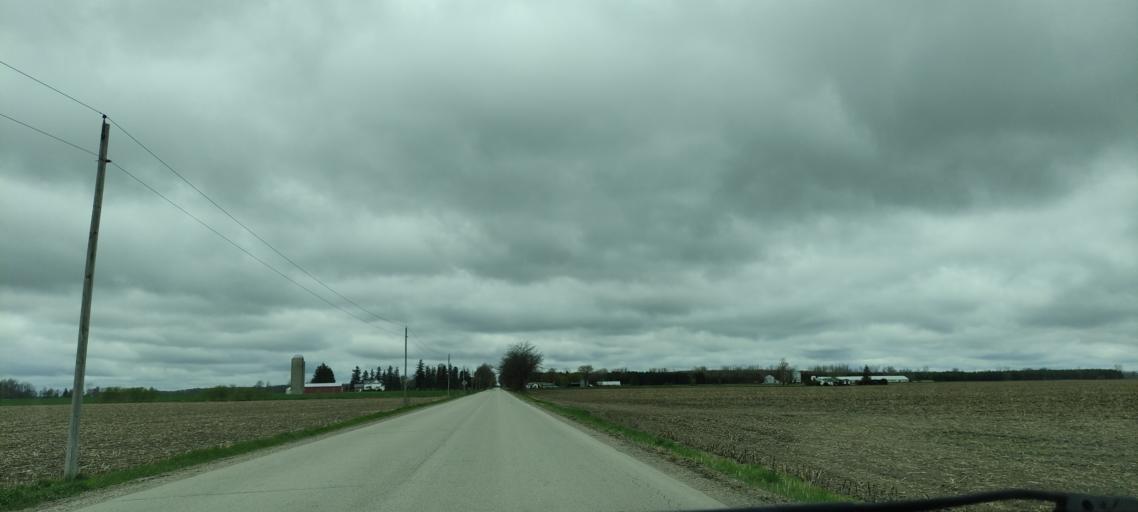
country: CA
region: Ontario
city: Stratford
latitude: 43.4201
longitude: -80.9453
